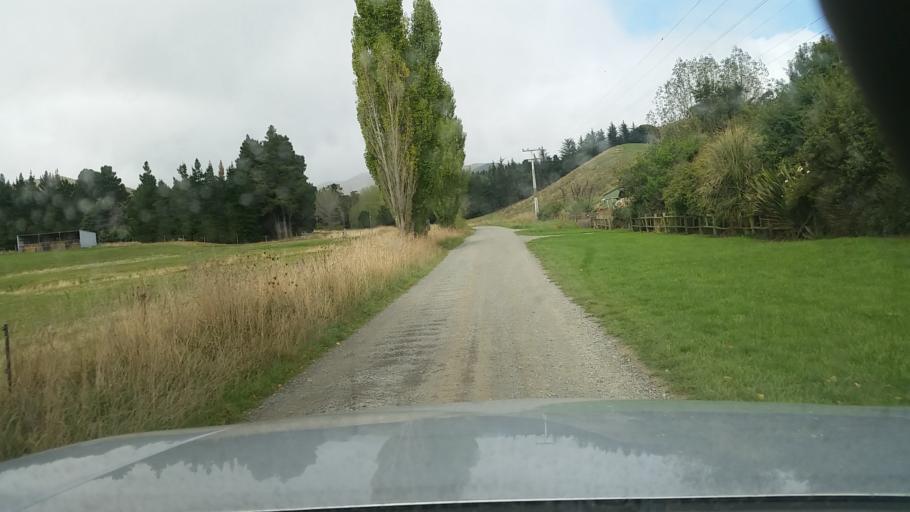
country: NZ
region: Marlborough
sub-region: Marlborough District
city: Blenheim
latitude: -41.7301
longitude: 173.9226
